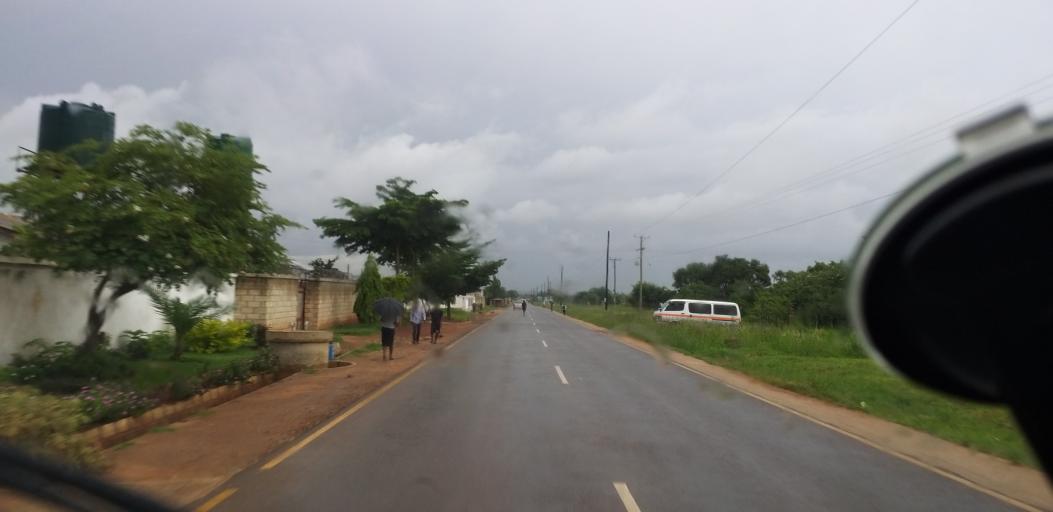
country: ZM
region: Lusaka
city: Lusaka
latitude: -15.5029
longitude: 28.3122
